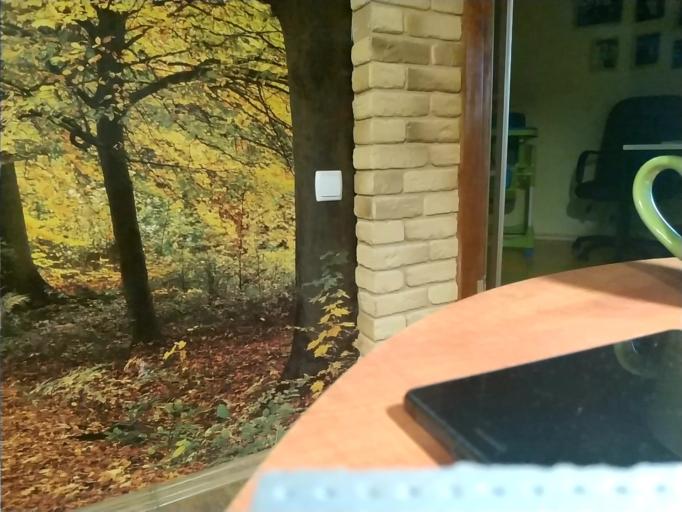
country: RU
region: Moskovskaya
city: Klin
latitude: 56.3573
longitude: 36.7526
